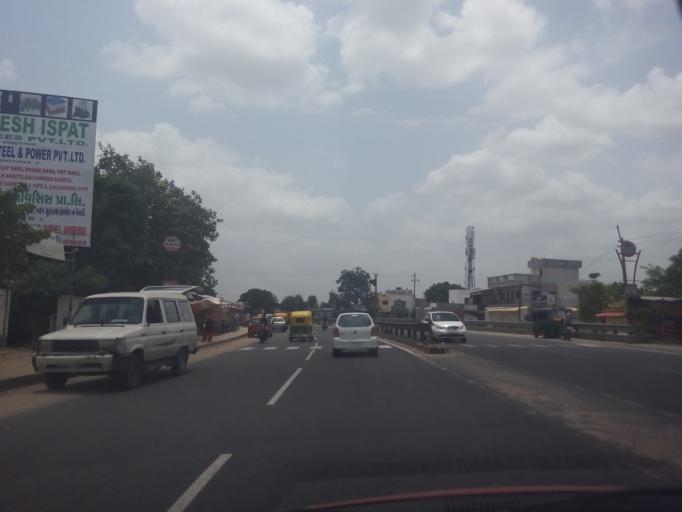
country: IN
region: Gujarat
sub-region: Ahmadabad
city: Sanand
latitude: 22.9845
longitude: 72.4354
